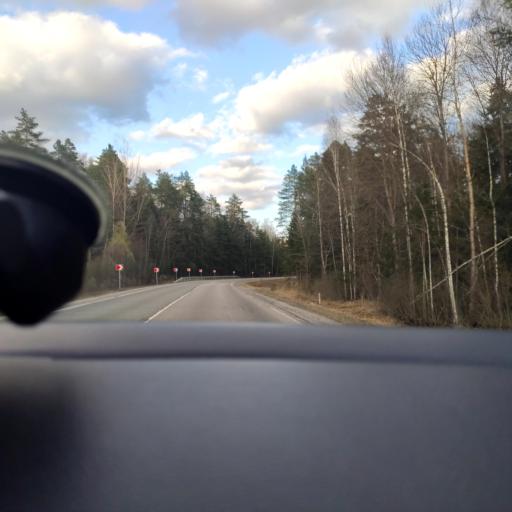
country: RU
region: Moskovskaya
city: Shaturtorf
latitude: 55.4301
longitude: 39.3580
